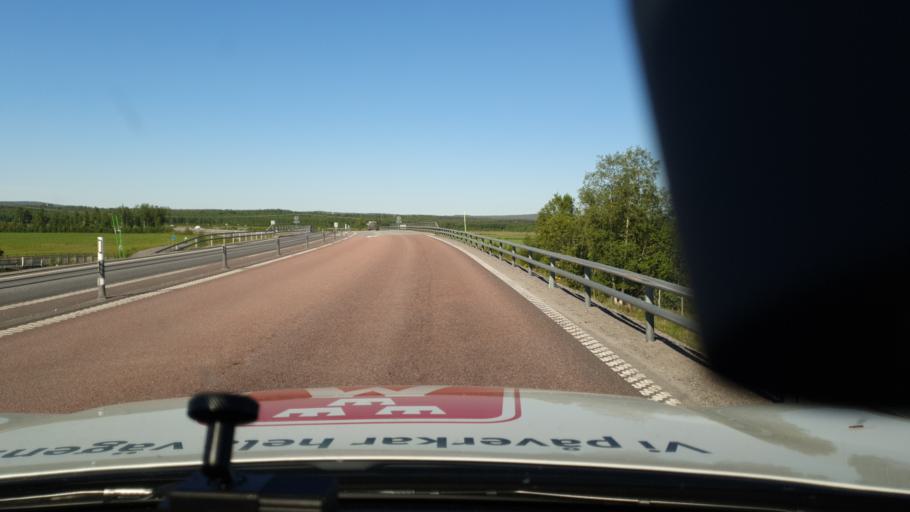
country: SE
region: Vaesterbotten
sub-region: Umea Kommun
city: Roback
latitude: 63.8567
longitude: 20.2019
